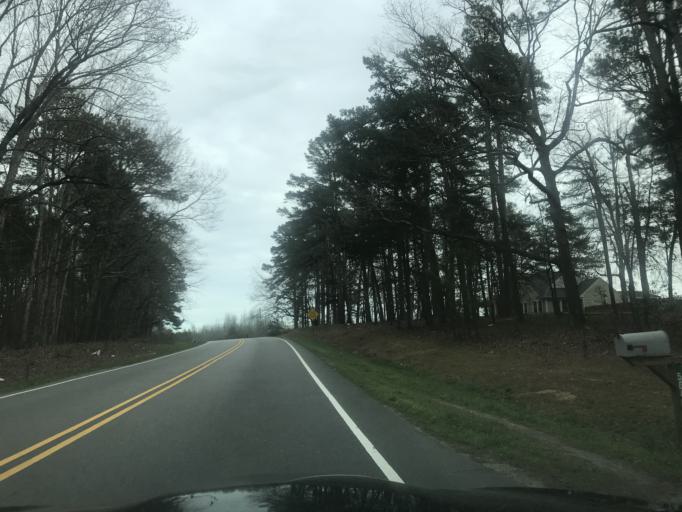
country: US
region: North Carolina
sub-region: Franklin County
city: Franklinton
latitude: 36.0948
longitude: -78.4154
